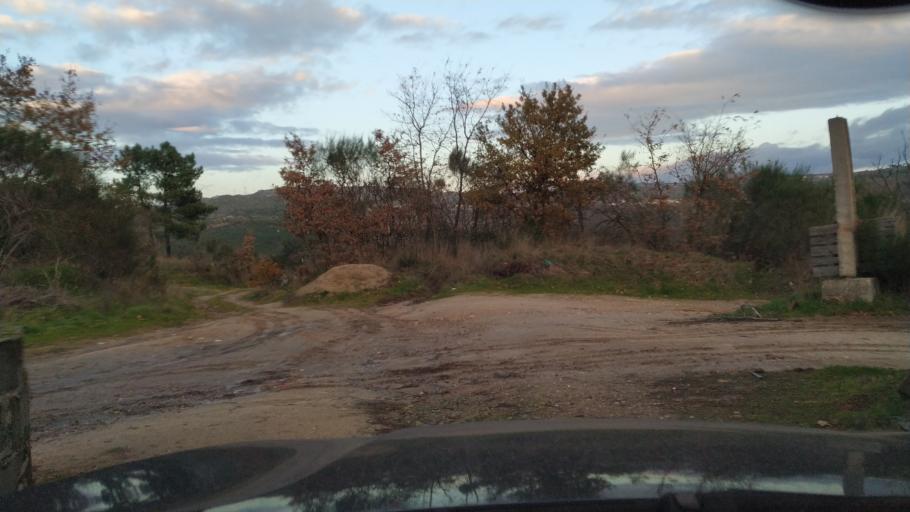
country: PT
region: Vila Real
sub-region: Vila Real
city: Vila Real
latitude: 41.3487
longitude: -7.7186
